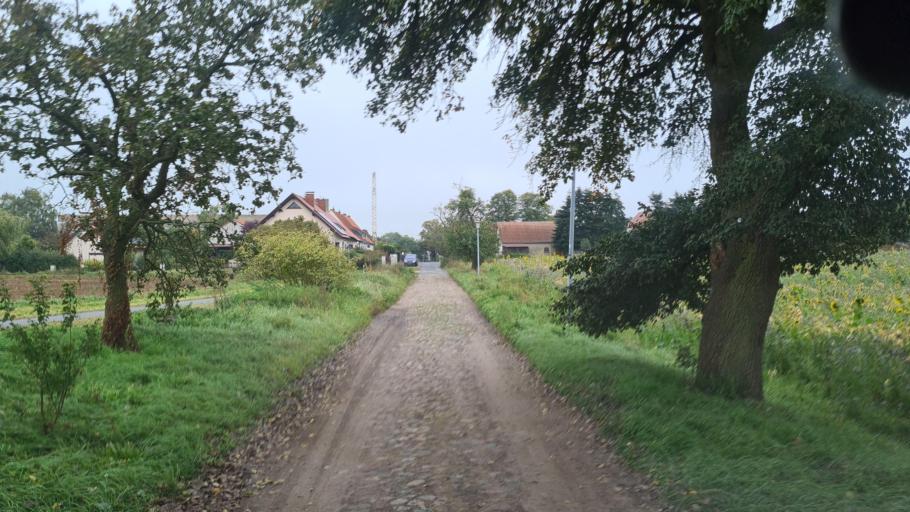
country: DE
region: Brandenburg
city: Furstenwalde
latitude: 52.4058
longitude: 14.0388
